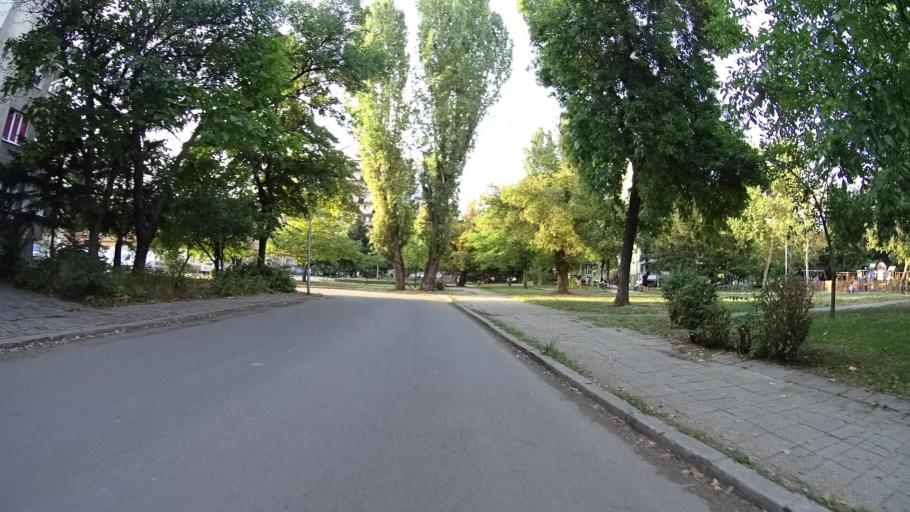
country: BG
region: Plovdiv
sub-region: Obshtina Plovdiv
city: Plovdiv
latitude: 42.1316
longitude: 24.7470
